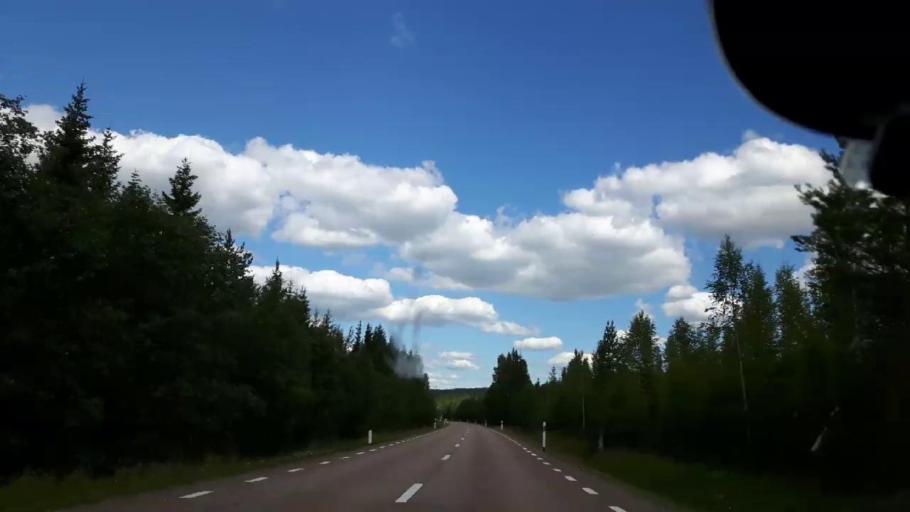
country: SE
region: Jaemtland
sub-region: Ragunda Kommun
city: Hammarstrand
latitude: 62.8976
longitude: 16.6962
